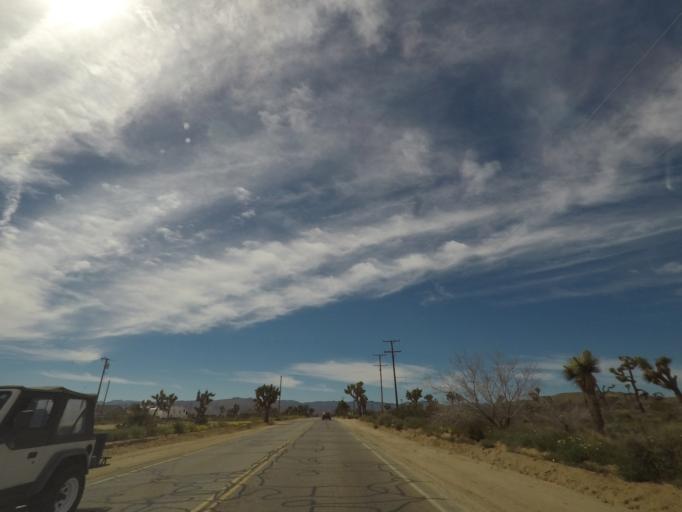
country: US
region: California
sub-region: San Bernardino County
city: Joshua Tree
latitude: 34.1756
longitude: -116.3696
